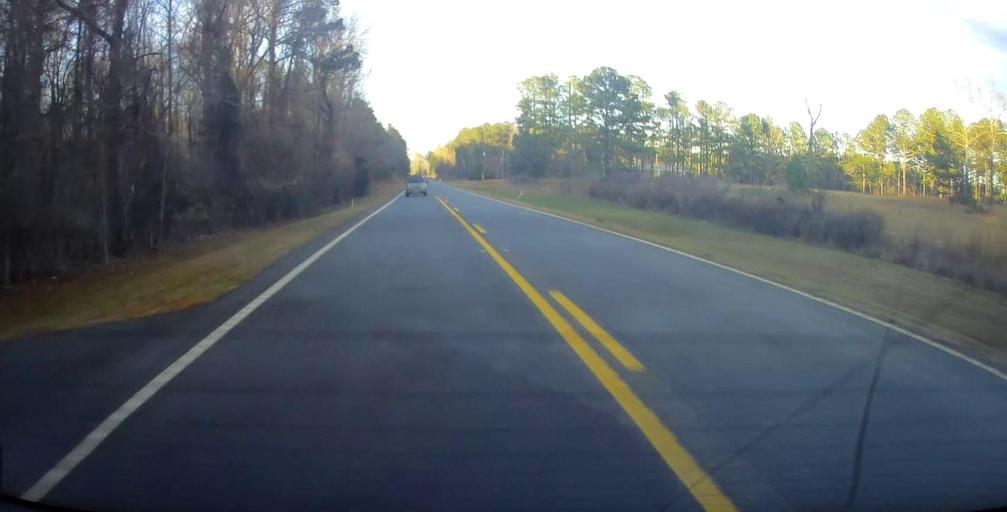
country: US
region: Georgia
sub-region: Talbot County
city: Sardis
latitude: 32.6993
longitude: -84.7004
